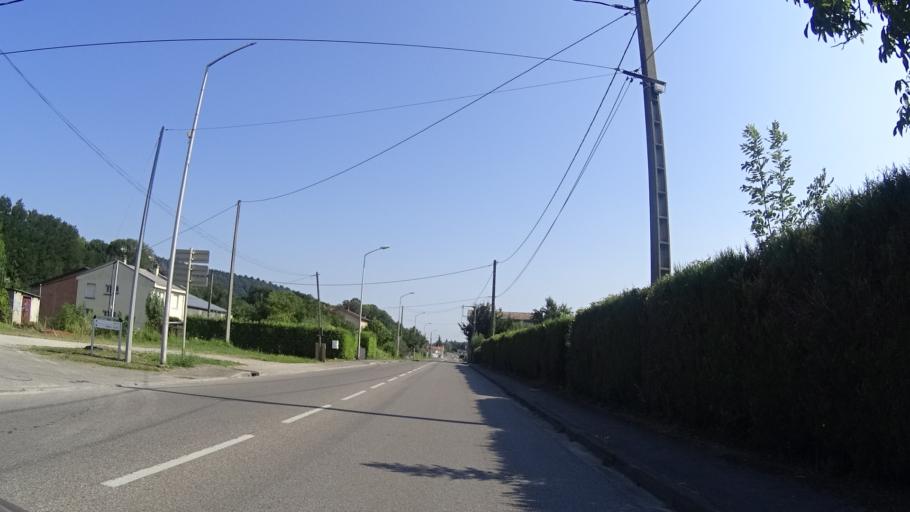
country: FR
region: Midi-Pyrenees
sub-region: Departement de l'Ariege
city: Lavelanet
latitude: 42.9436
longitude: 1.8571
